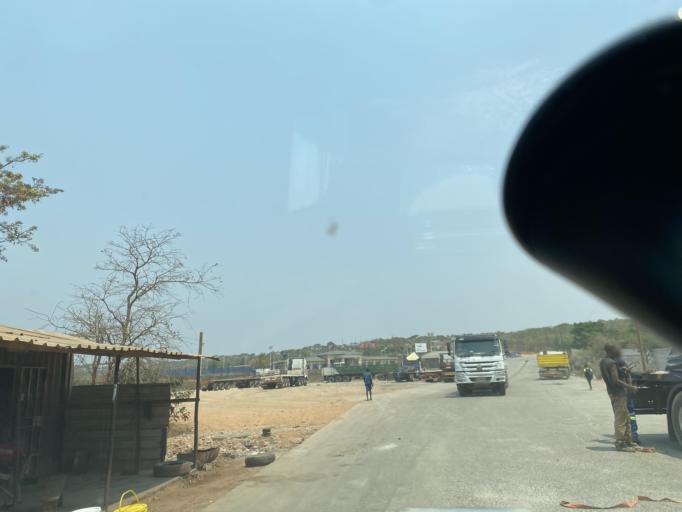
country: ZM
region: Lusaka
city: Lusaka
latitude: -15.5518
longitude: 28.4832
